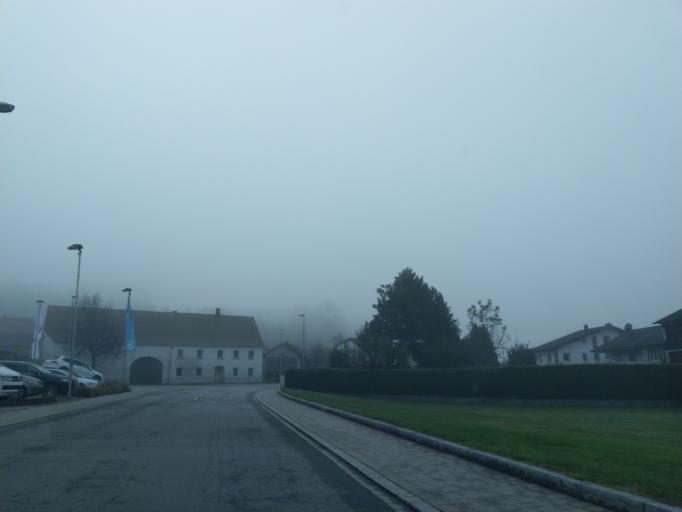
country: DE
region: Bavaria
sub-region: Lower Bavaria
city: Hengersberg
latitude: 48.7799
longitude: 13.0525
